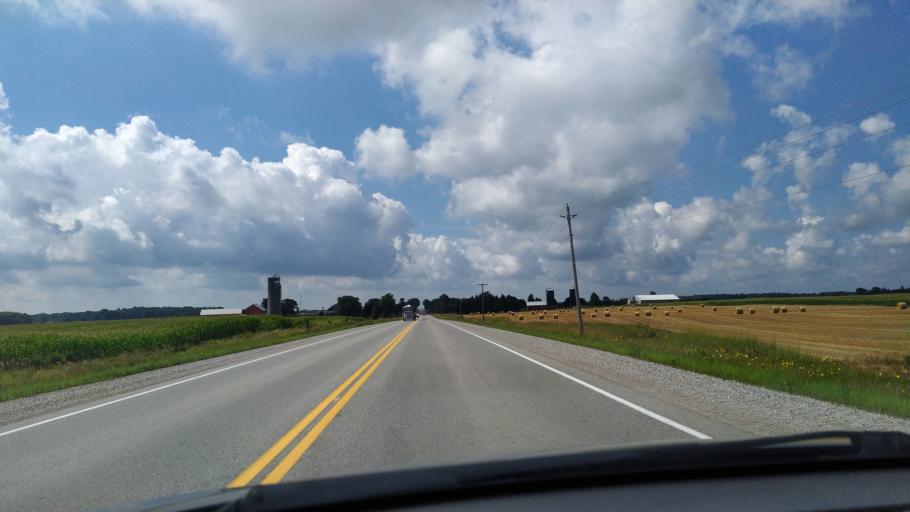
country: CA
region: Ontario
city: Huron East
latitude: 43.4304
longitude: -81.2300
